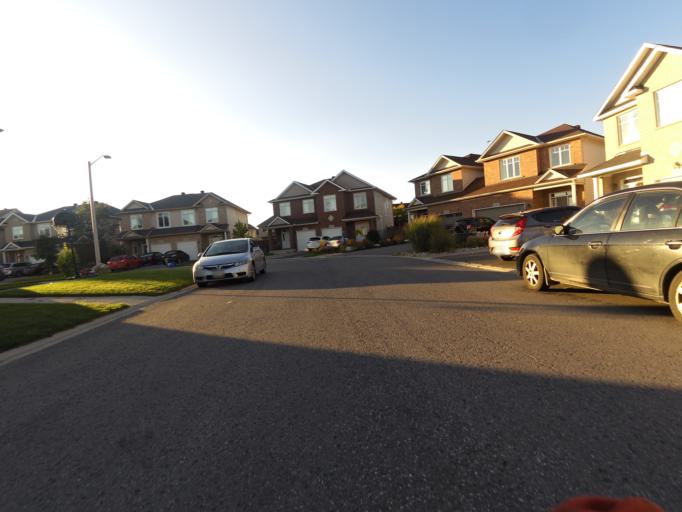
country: CA
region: Ontario
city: Bells Corners
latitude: 45.3622
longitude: -75.9276
